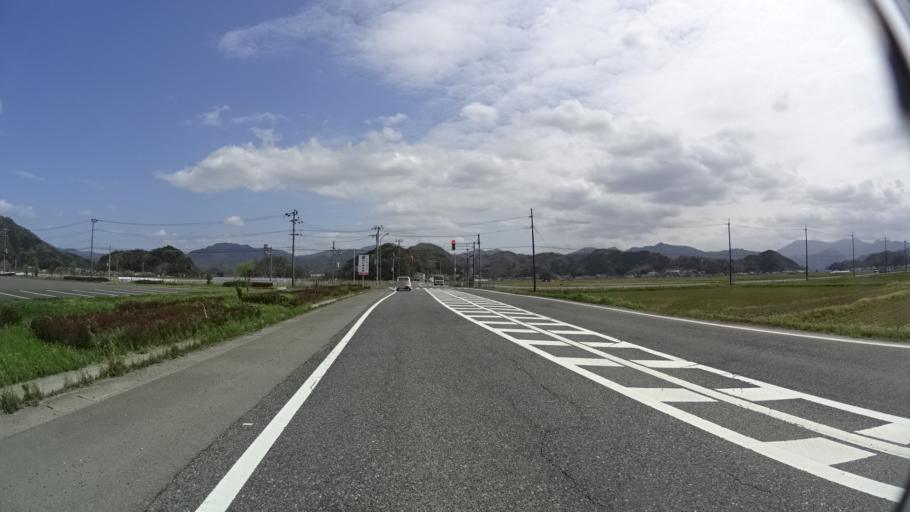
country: JP
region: Hyogo
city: Toyooka
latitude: 35.5074
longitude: 134.8394
